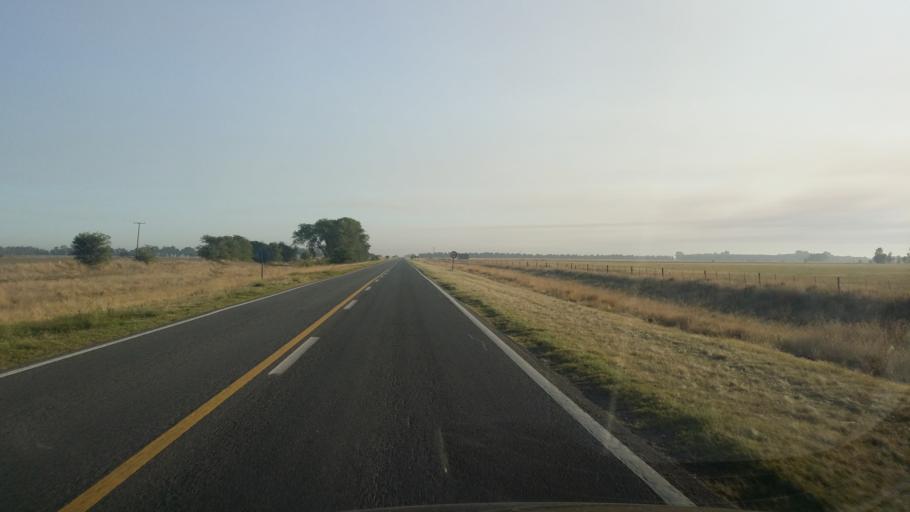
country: AR
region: La Pampa
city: Santa Rosa
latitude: -36.4863
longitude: -64.2800
